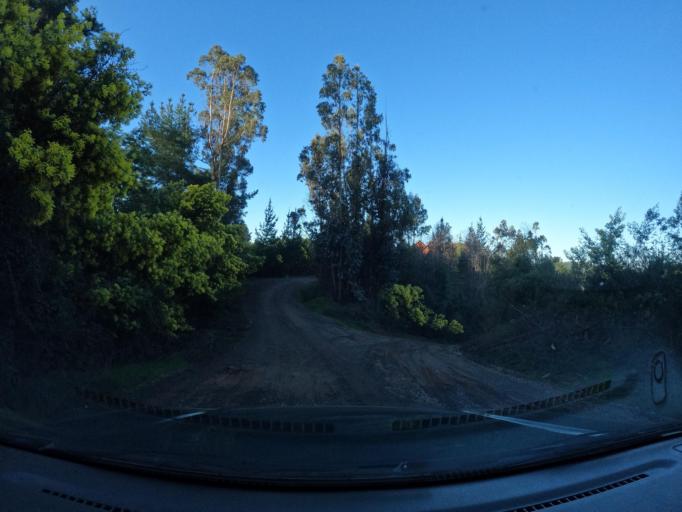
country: CL
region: Biobio
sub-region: Provincia de Concepcion
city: Chiguayante
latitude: -37.0163
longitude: -72.8395
